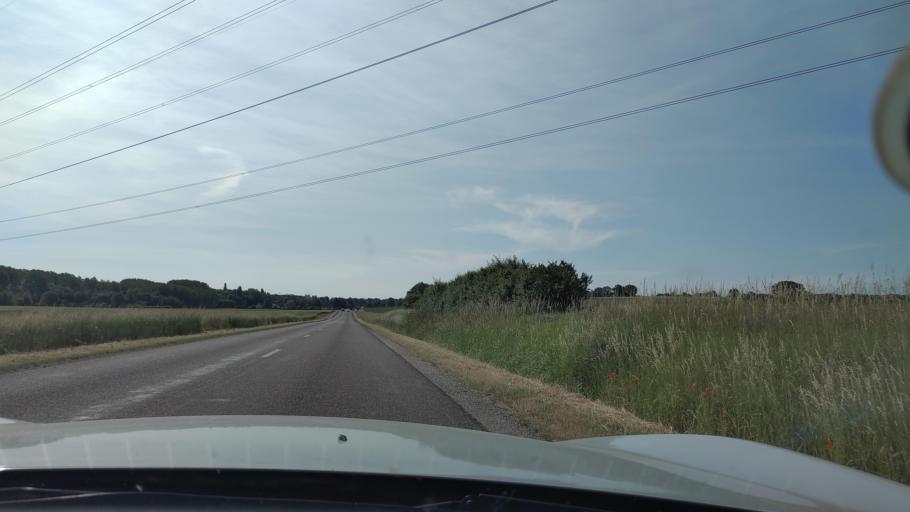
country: FR
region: Champagne-Ardenne
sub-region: Departement de l'Aube
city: Nogent-sur-Seine
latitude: 48.4584
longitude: 3.5975
